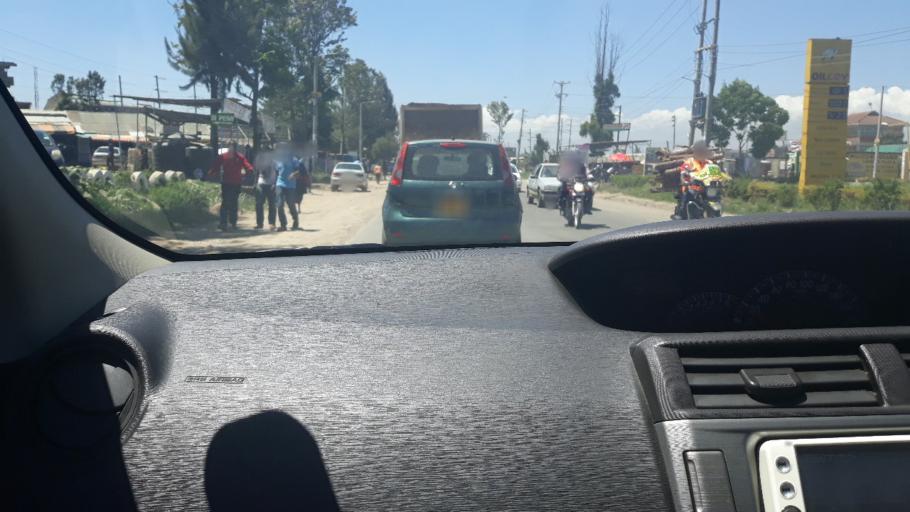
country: KE
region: Nairobi Area
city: Pumwani
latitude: -1.2757
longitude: 36.8891
